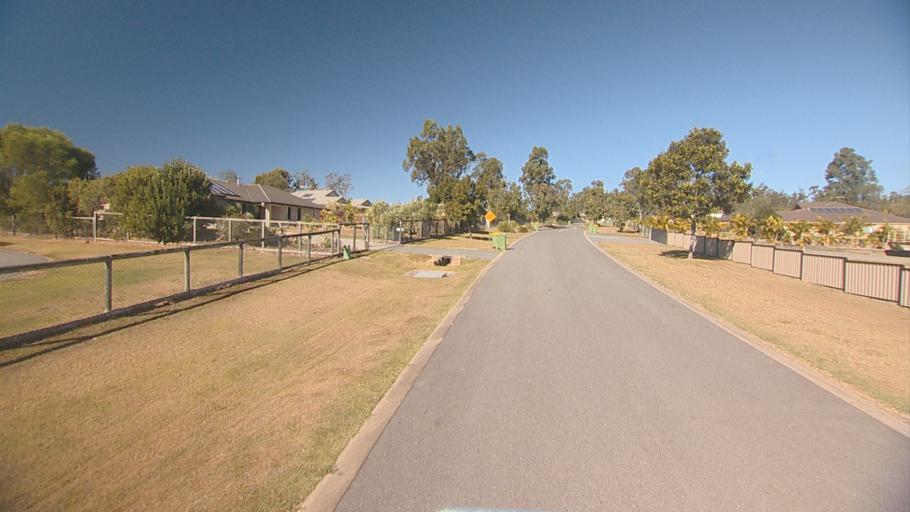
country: AU
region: Queensland
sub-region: Logan
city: North Maclean
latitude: -27.7573
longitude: 152.9622
